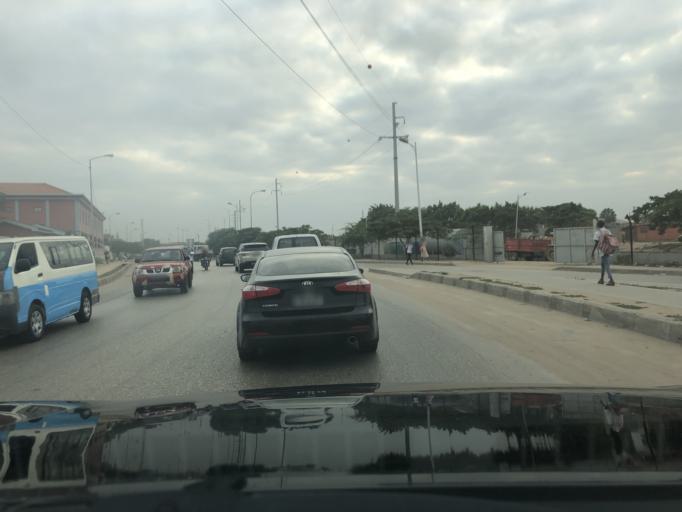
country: AO
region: Luanda
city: Luanda
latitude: -8.8389
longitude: 13.2536
